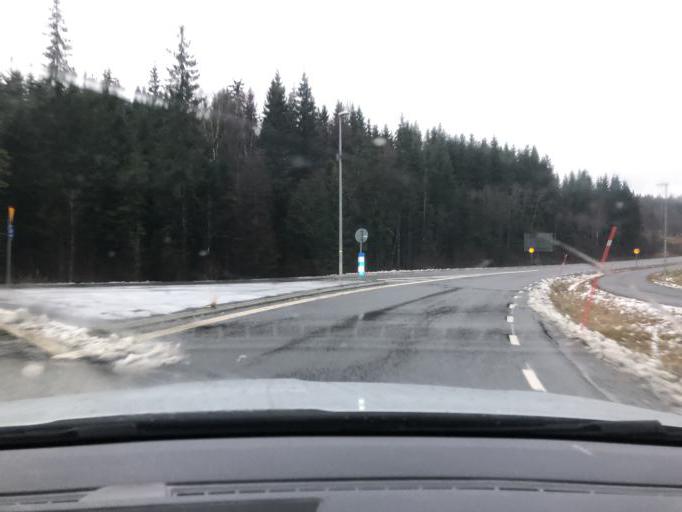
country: SE
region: Vaestra Goetaland
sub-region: Ulricehamns Kommun
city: Ulricehamn
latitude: 57.8206
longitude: 13.2857
